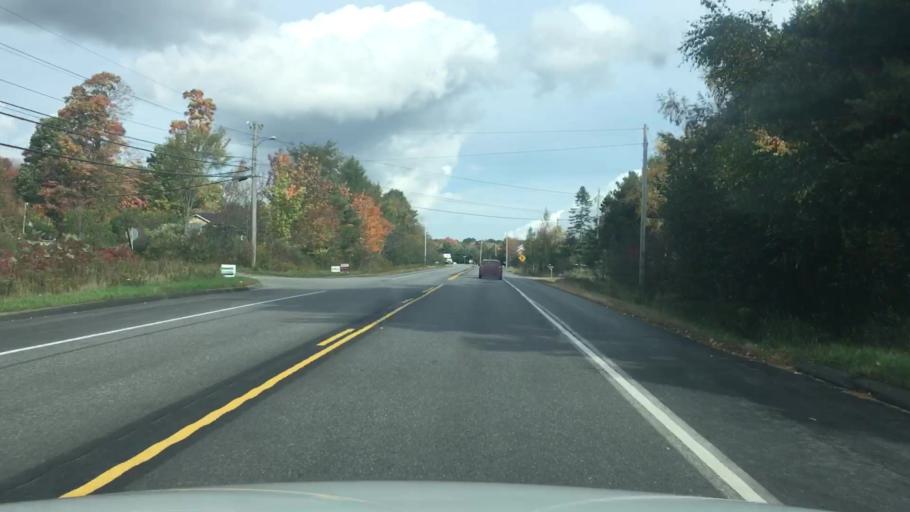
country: US
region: Maine
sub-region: Knox County
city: Rockland
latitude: 44.1512
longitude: -69.1148
